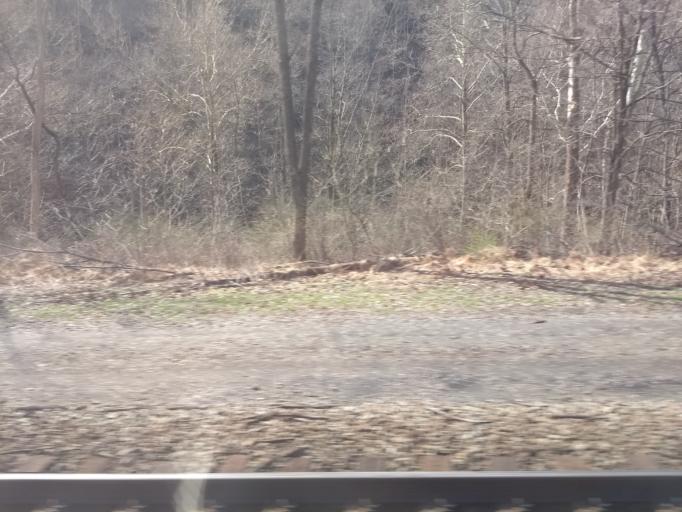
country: US
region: Pennsylvania
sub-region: Blair County
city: Tyrone
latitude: 40.6276
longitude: -78.1781
